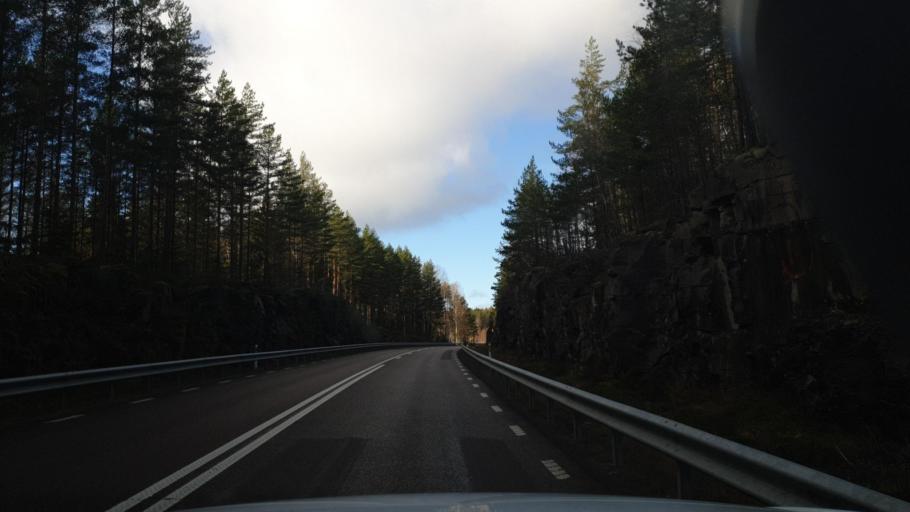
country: SE
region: Vaermland
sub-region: Arvika Kommun
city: Arvika
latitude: 59.5845
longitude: 12.6667
